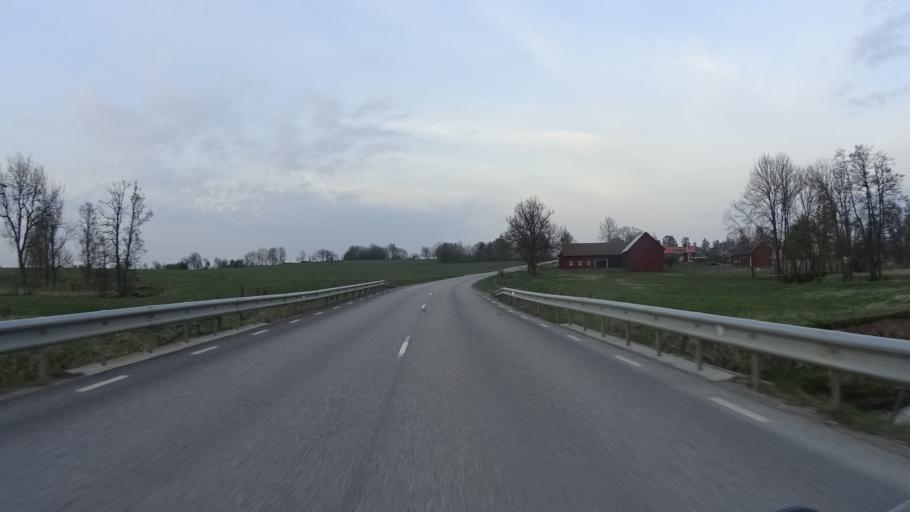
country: SE
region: Vaestra Goetaland
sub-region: Gotene Kommun
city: Kallby
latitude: 58.5134
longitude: 13.3175
